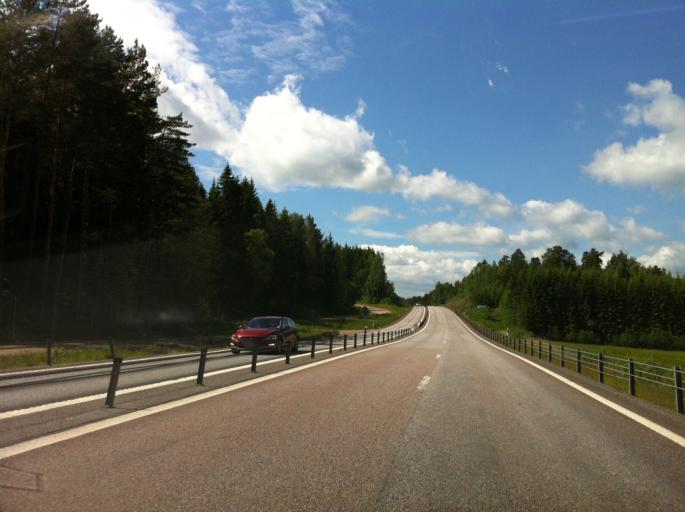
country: SE
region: Vaermland
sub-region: Grums Kommun
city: Slottsbron
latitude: 59.3139
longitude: 13.0930
